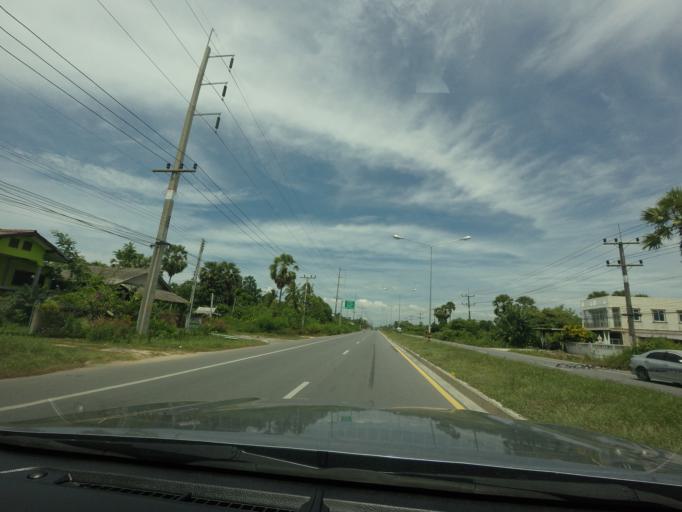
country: TH
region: Songkhla
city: Ranot
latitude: 7.7436
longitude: 100.3636
